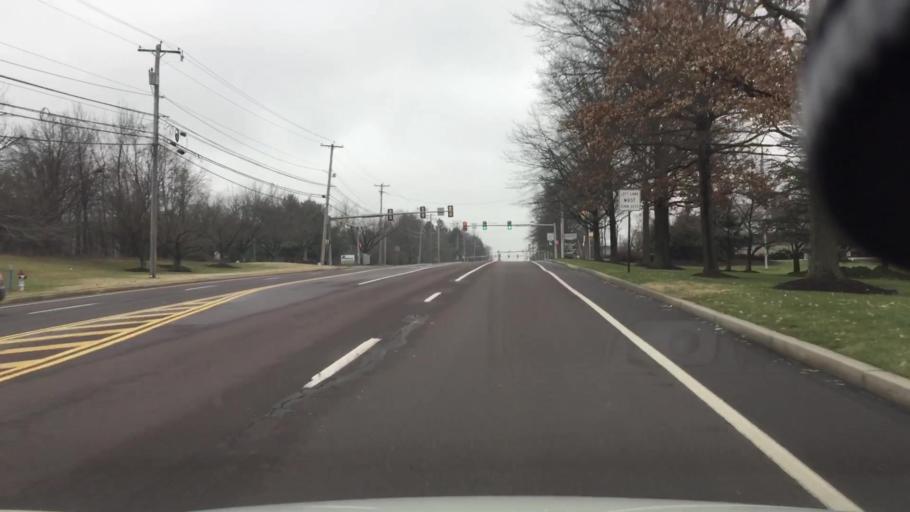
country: US
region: Pennsylvania
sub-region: Montgomery County
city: Horsham
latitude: 40.1679
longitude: -75.1452
